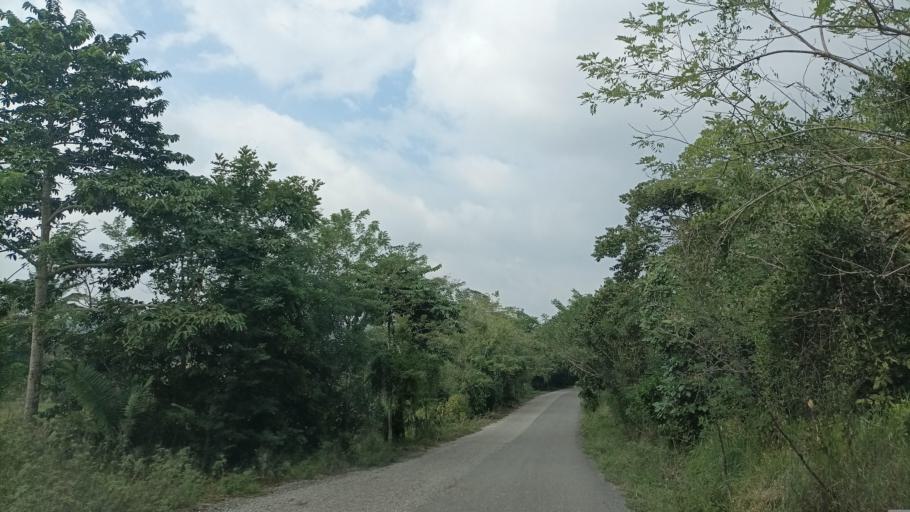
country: MX
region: Veracruz
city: Allende
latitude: 18.1011
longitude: -94.2942
